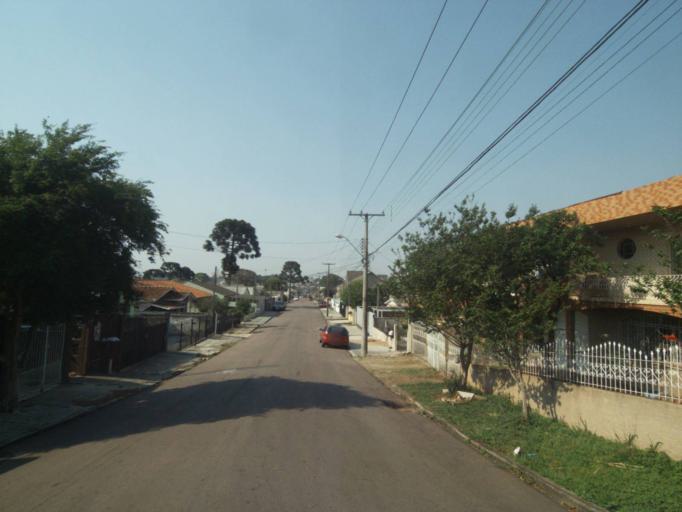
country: BR
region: Parana
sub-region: Sao Jose Dos Pinhais
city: Sao Jose dos Pinhais
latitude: -25.5134
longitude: -49.2821
